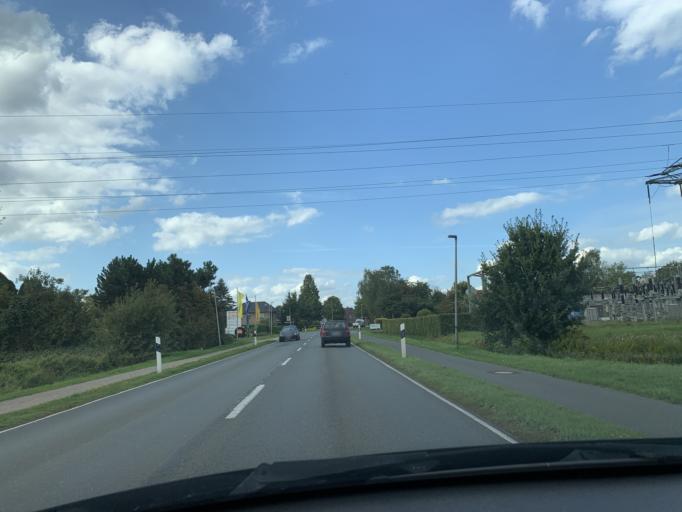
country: DE
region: Lower Saxony
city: Bad Zwischenahn
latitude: 53.1738
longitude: 7.9965
